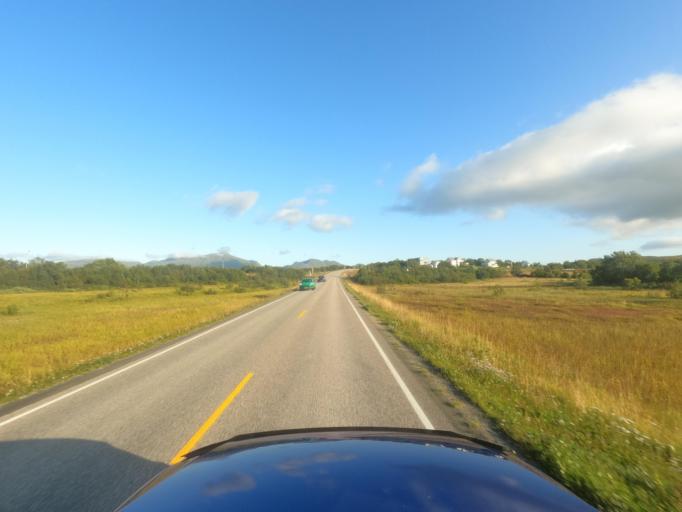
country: NO
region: Nordland
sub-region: Vestvagoy
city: Gravdal
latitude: 68.1517
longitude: 13.5403
